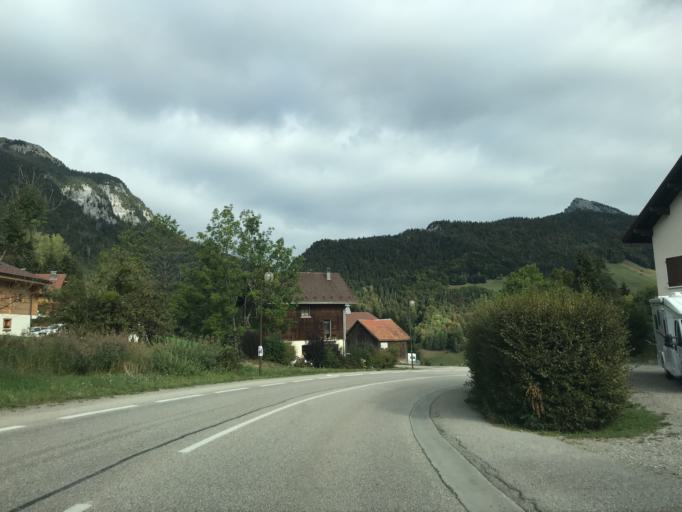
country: FR
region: Rhone-Alpes
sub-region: Departement de la Haute-Savoie
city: Saint-Jean-de-Sixt
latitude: 45.9243
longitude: 6.4095
